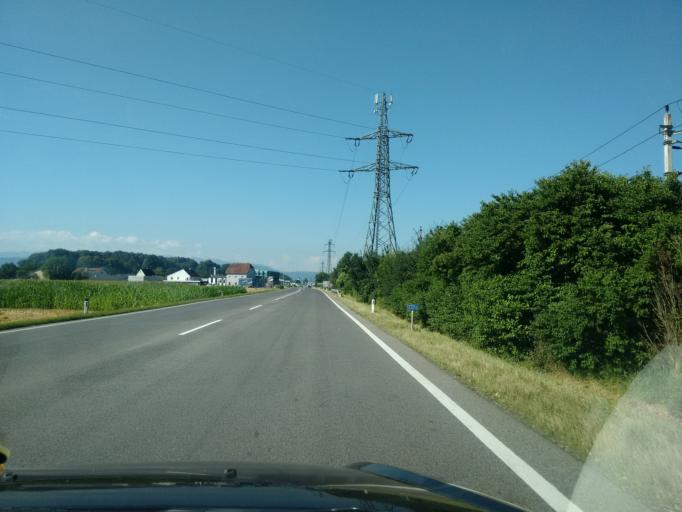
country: AT
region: Upper Austria
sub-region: Politischer Bezirk Vocklabruck
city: Redlham
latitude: 48.0300
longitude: 13.7375
